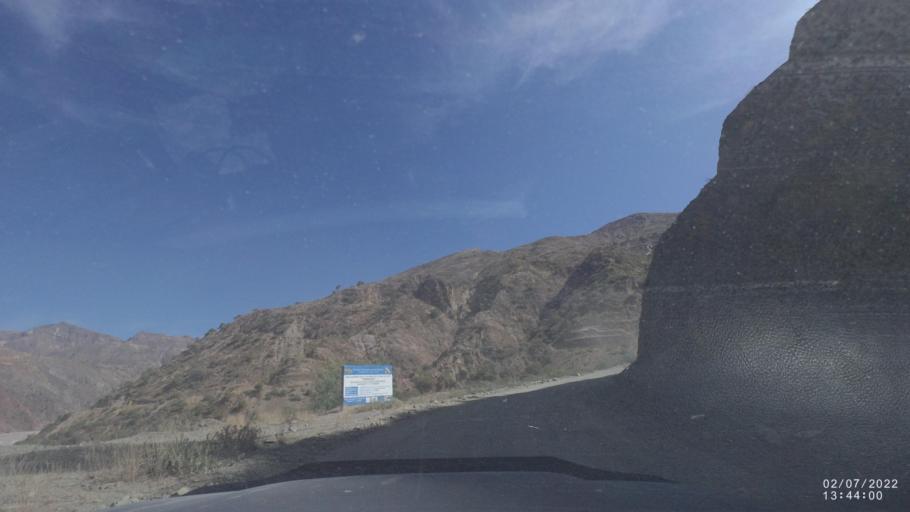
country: BO
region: Cochabamba
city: Irpa Irpa
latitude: -17.8060
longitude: -66.3626
